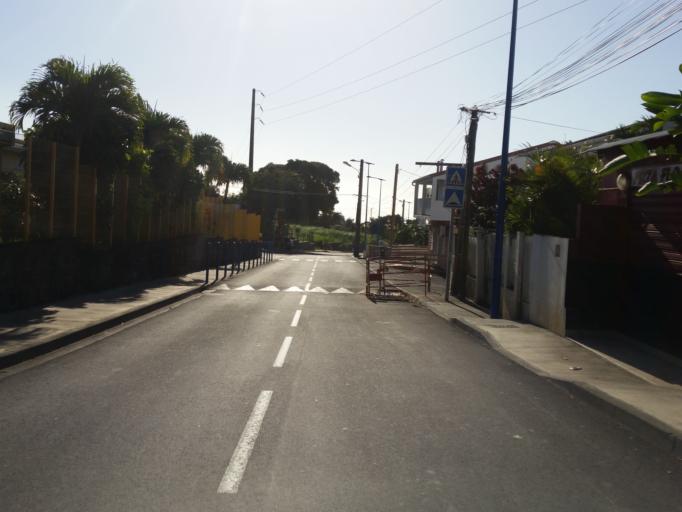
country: RE
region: Reunion
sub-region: Reunion
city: Sainte-Marie
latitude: -20.9257
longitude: 55.5197
